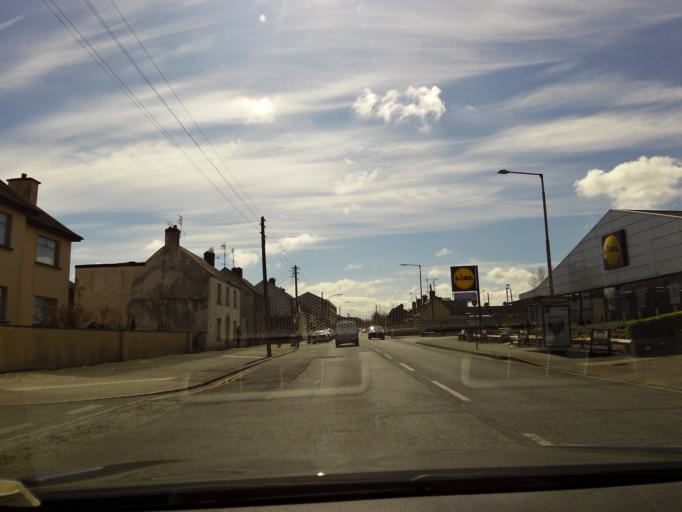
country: IE
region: Leinster
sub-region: Wicklow
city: Arklow
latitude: 52.7959
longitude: -6.1623
